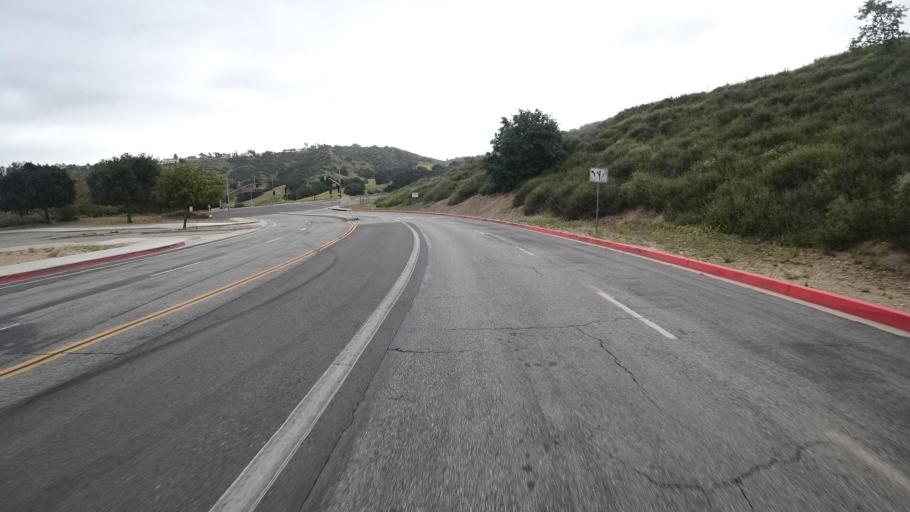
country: US
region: California
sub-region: San Bernardino County
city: Chino Hills
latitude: 34.0217
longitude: -117.7722
